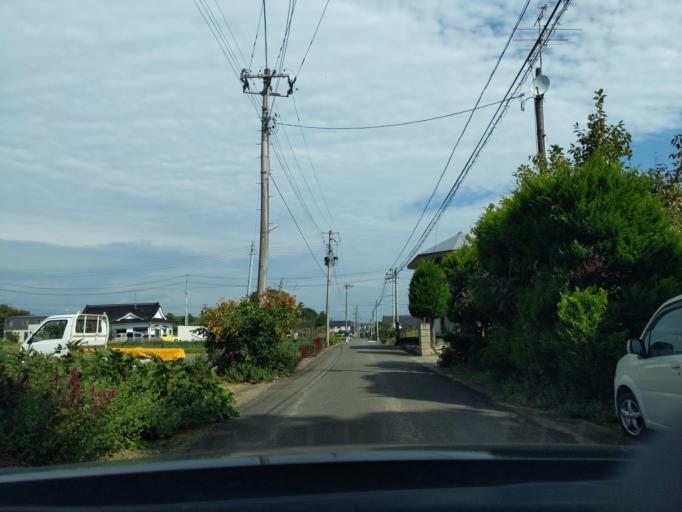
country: JP
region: Fukushima
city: Koriyama
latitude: 37.3942
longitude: 140.2694
